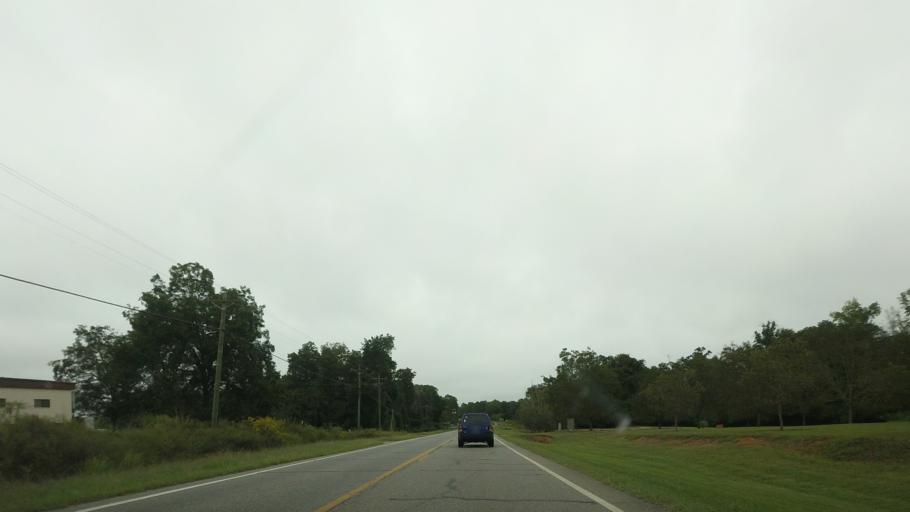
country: US
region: Georgia
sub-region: Irwin County
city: Ocilla
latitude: 31.5786
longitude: -83.2524
